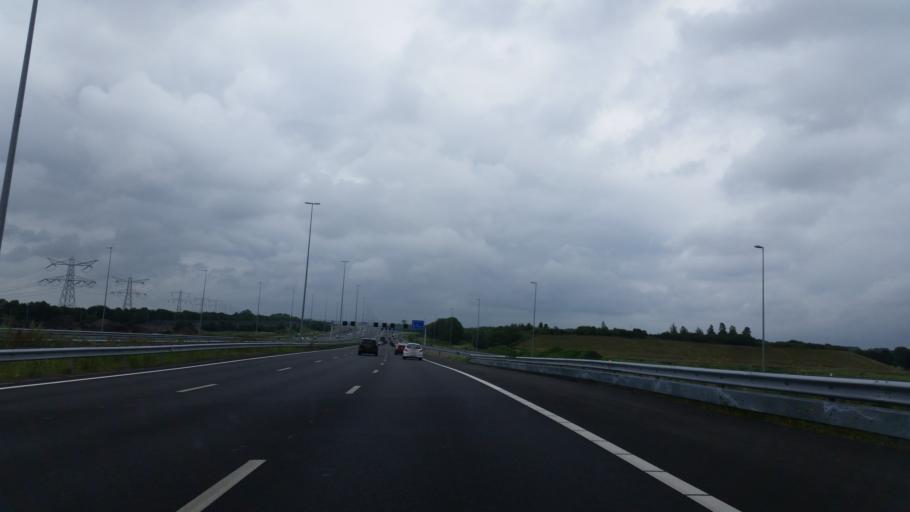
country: NL
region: North Holland
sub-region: Gemeente Naarden
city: Naarden
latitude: 52.3151
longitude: 5.1145
